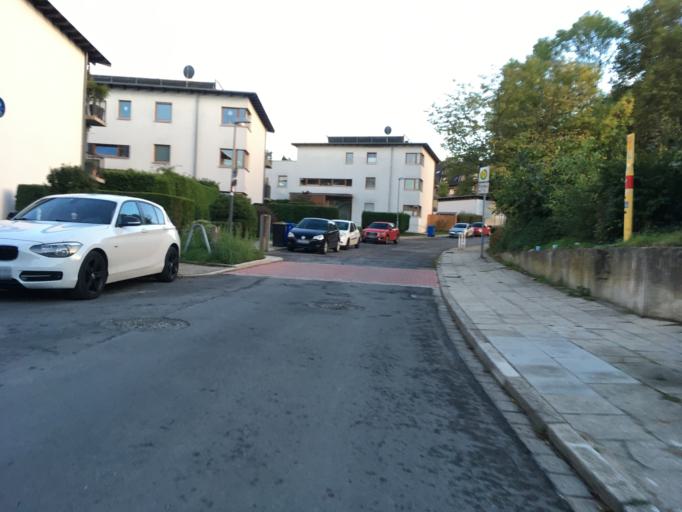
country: DE
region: North Rhine-Westphalia
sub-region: Regierungsbezirk Munster
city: Bottrop
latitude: 51.4844
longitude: 6.9262
